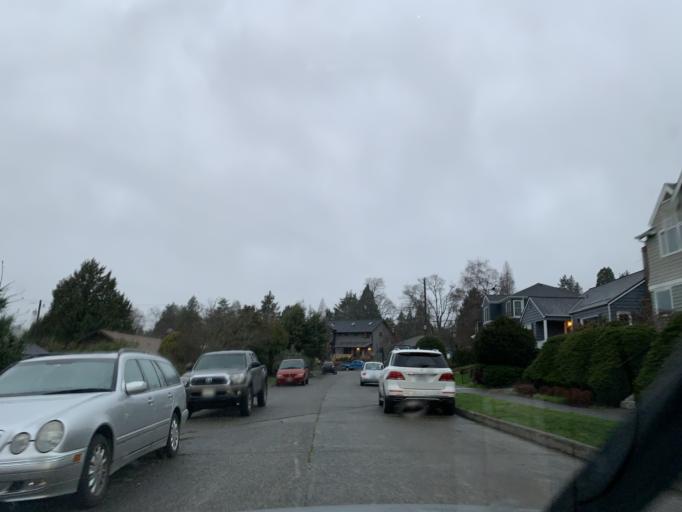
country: US
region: Washington
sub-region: King County
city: Yarrow Point
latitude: 47.6716
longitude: -122.2783
